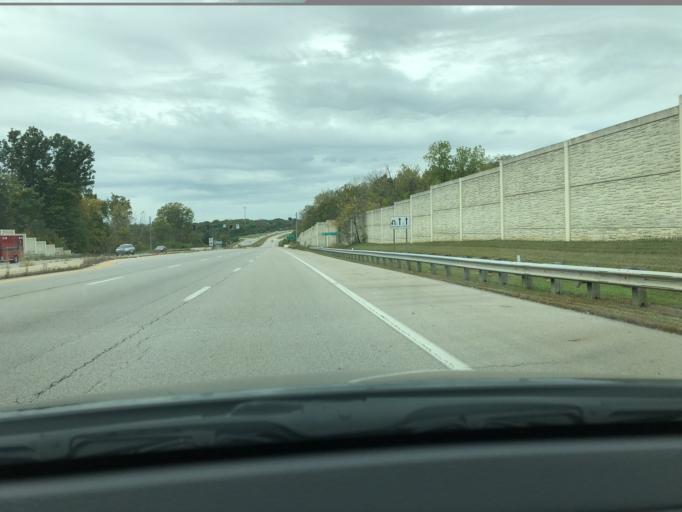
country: US
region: Ohio
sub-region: Franklin County
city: Huber Ridge
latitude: 40.0819
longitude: -82.9171
